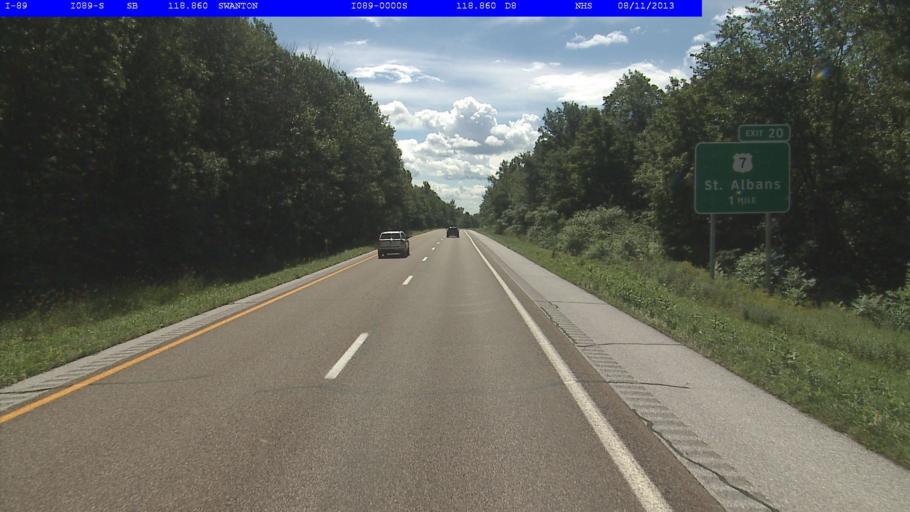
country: US
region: Vermont
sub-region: Franklin County
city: Saint Albans
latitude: 44.8607
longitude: -73.0825
